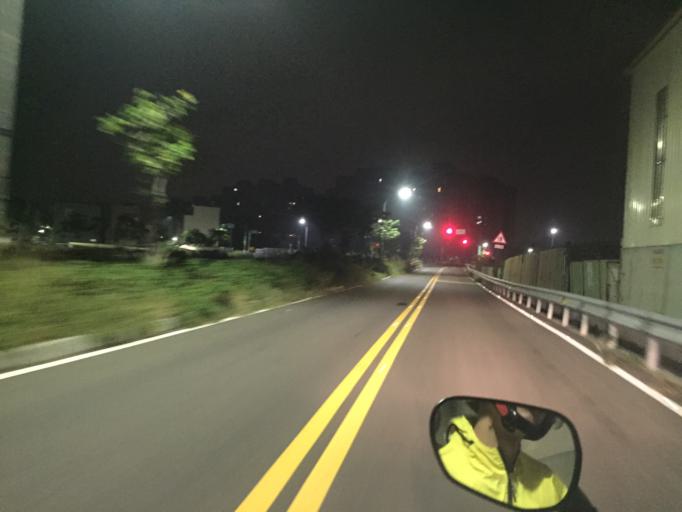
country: TW
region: Taiwan
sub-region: Hsinchu
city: Hsinchu
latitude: 24.8013
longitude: 120.9492
